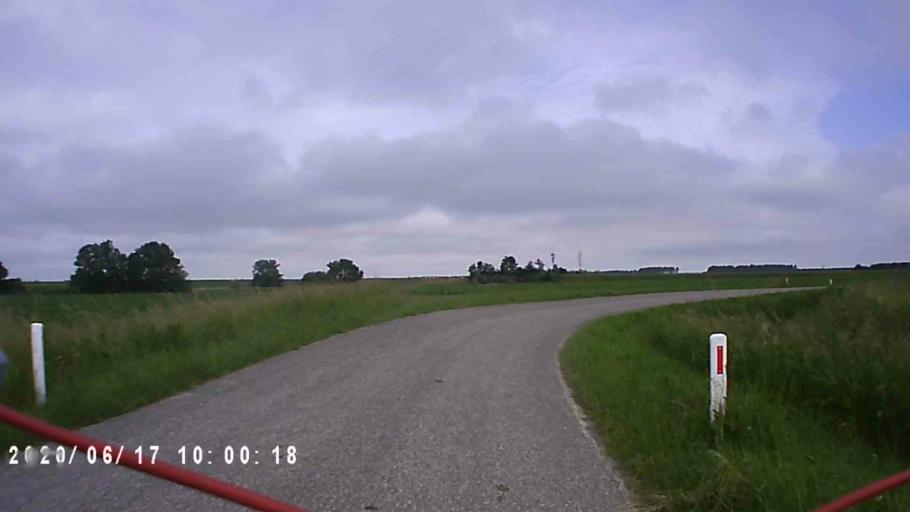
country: NL
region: Groningen
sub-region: Gemeente De Marne
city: Ulrum
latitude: 53.3665
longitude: 6.2840
